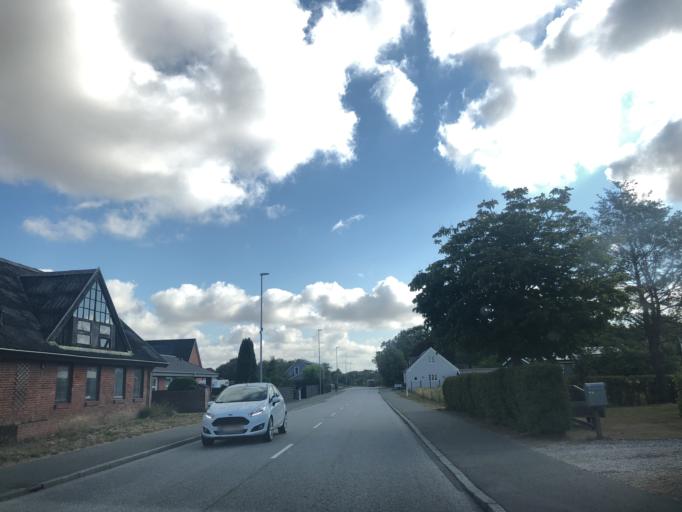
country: DK
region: Central Jutland
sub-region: Skive Kommune
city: Skive
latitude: 56.6449
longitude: 8.9267
